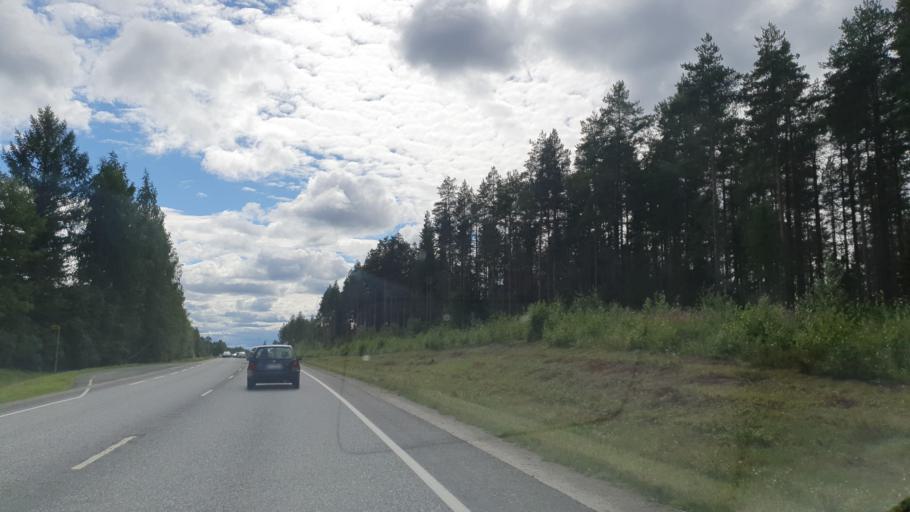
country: FI
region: Kainuu
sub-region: Kajaani
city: Kajaani
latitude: 64.1649
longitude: 27.5267
